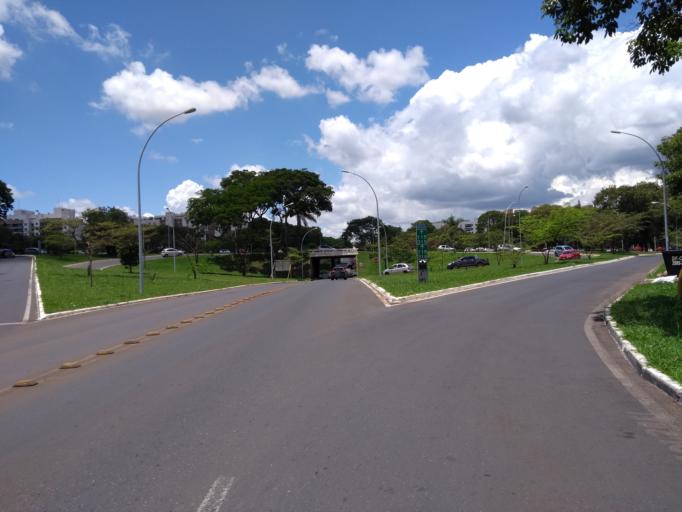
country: BR
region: Federal District
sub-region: Brasilia
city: Brasilia
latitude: -15.7390
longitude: -47.8898
